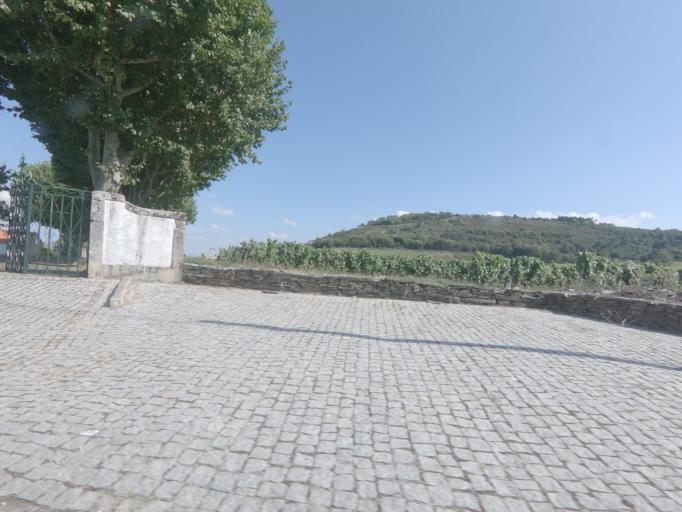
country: PT
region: Vila Real
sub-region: Sabrosa
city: Vilela
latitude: 41.2299
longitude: -7.5661
